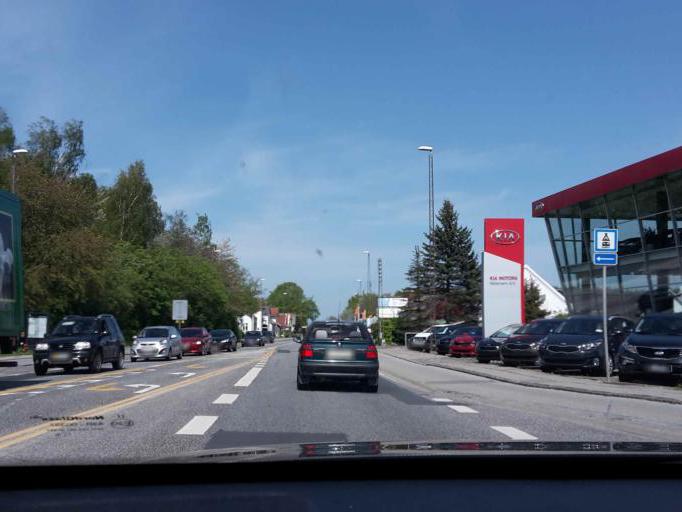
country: DK
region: South Denmark
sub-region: Odense Kommune
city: Odense
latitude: 55.3694
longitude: 10.3937
